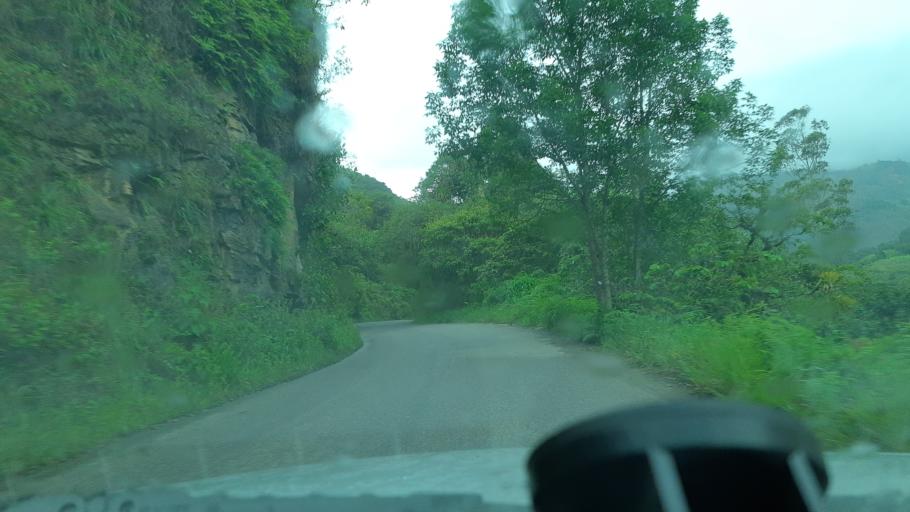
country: CO
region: Boyaca
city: Chinavita
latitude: 5.1911
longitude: -73.3813
